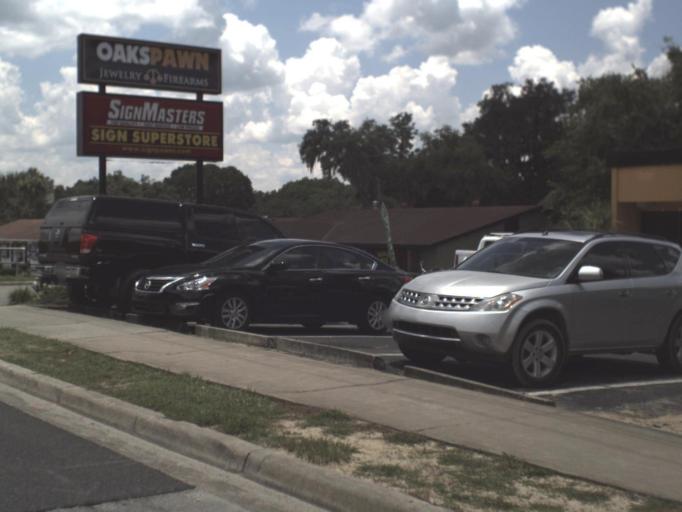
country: US
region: Florida
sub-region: Alachua County
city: Gainesville
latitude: 29.6293
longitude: -82.3727
